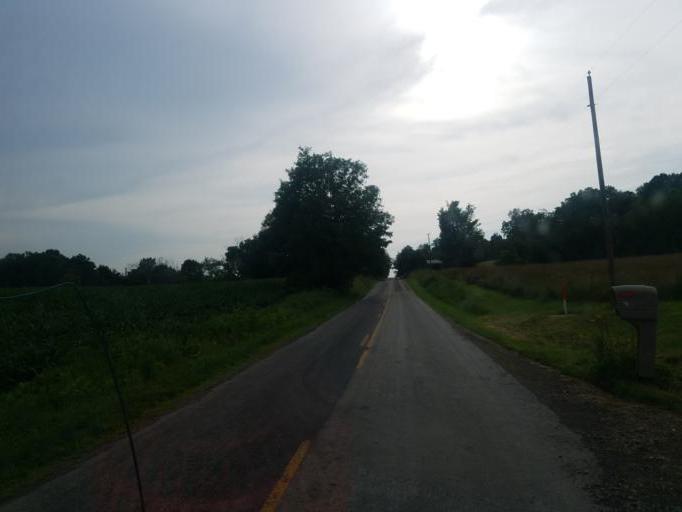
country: US
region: Ohio
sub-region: Wayne County
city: West Salem
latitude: 40.9009
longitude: -82.1423
